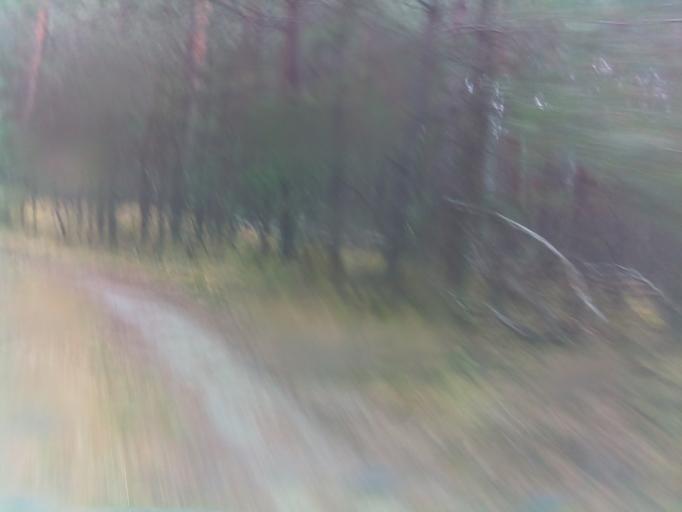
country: DE
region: Brandenburg
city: Jamlitz
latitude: 51.9825
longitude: 14.3810
